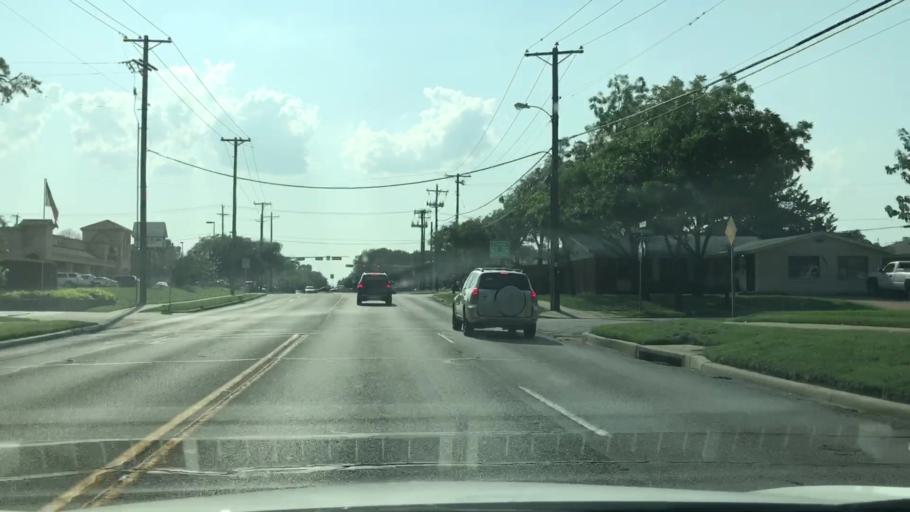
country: US
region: Texas
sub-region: Dallas County
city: Irving
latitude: 32.8443
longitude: -96.9495
